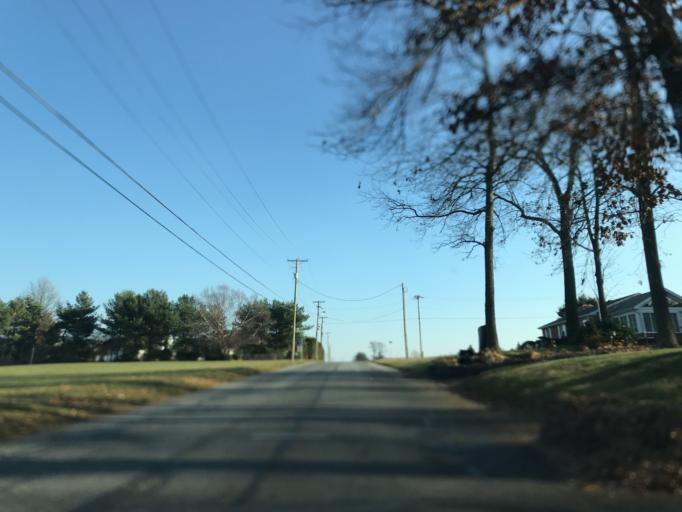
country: US
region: Pennsylvania
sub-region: York County
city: New Freedom
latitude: 39.7409
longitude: -76.6933
